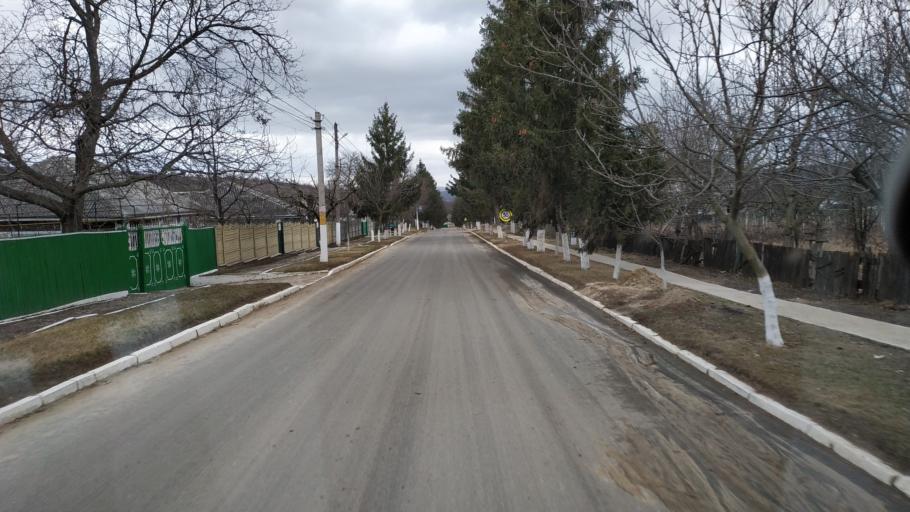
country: MD
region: Calarasi
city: Calarasi
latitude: 47.2056
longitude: 28.2441
